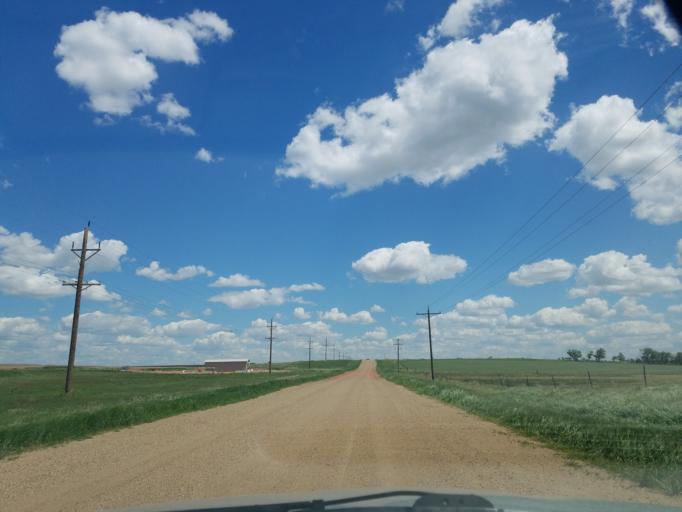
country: US
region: North Dakota
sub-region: McKenzie County
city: Watford City
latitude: 47.8195
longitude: -103.5653
